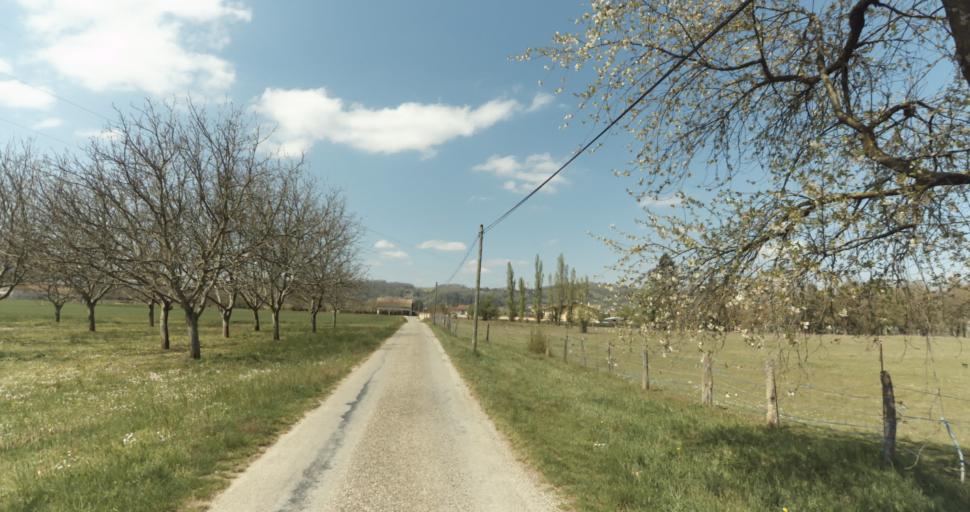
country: FR
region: Rhone-Alpes
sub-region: Departement de l'Isere
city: Saint-Marcellin
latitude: 45.1368
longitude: 5.3140
